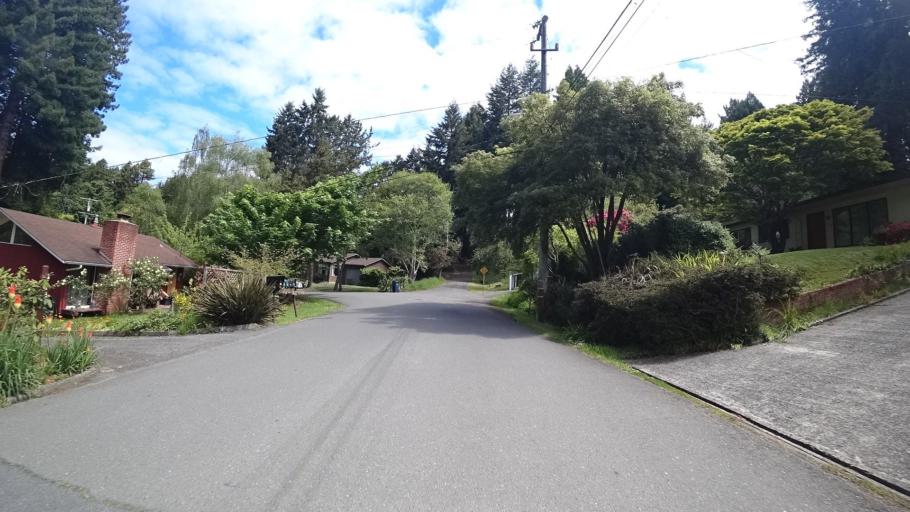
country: US
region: California
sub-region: Humboldt County
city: Arcata
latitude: 40.8662
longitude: -124.0701
